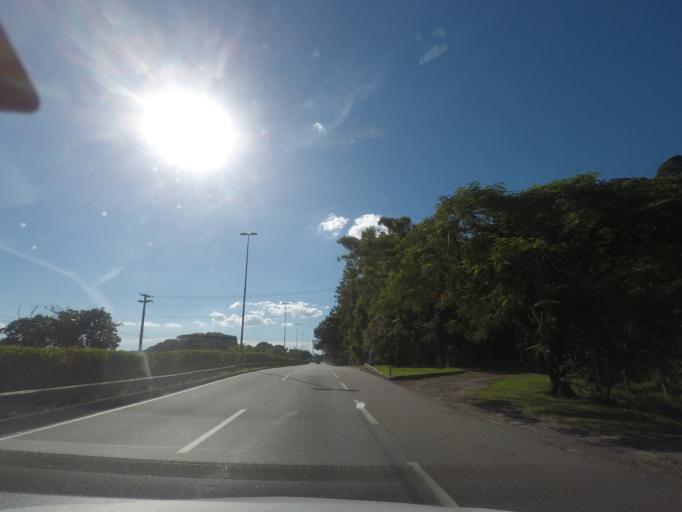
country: BR
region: Rio de Janeiro
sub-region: Sao Goncalo
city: Sao Goncalo
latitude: -22.6646
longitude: -43.1104
